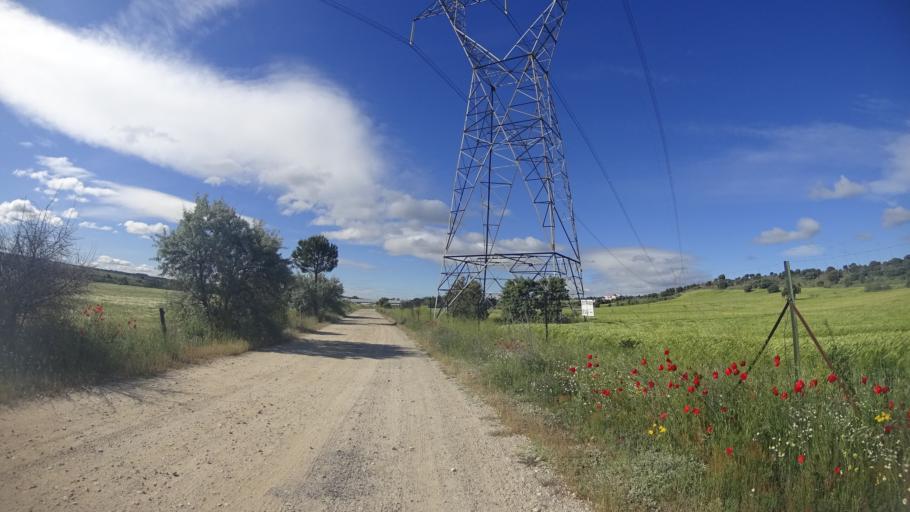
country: ES
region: Madrid
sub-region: Provincia de Madrid
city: Villanueva del Pardillo
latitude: 40.5020
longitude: -3.9400
